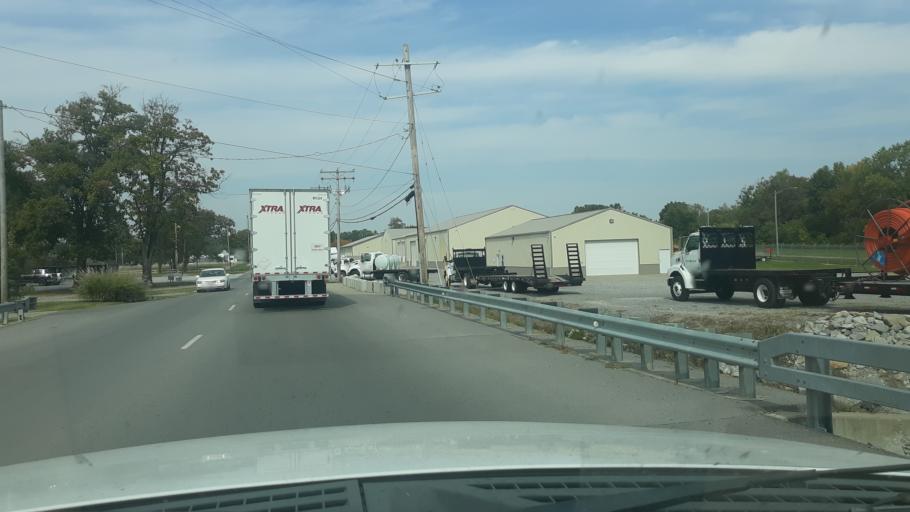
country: US
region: Illinois
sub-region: Saline County
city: Eldorado
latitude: 37.8090
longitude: -88.4347
